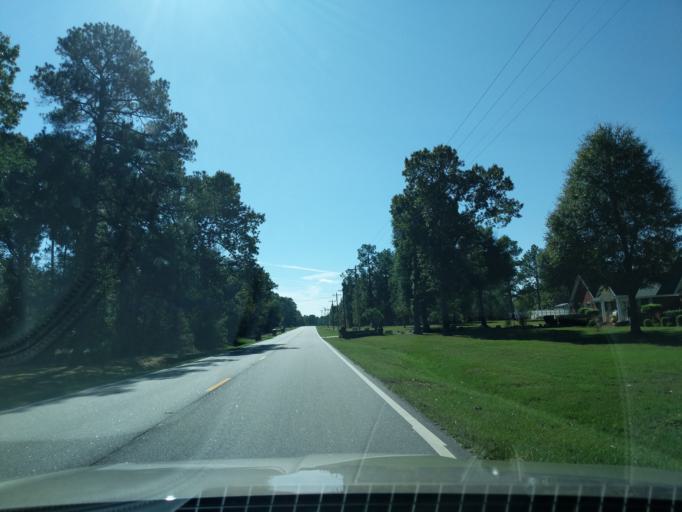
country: US
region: Georgia
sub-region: Richmond County
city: Hephzibah
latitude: 33.2654
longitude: -82.0093
